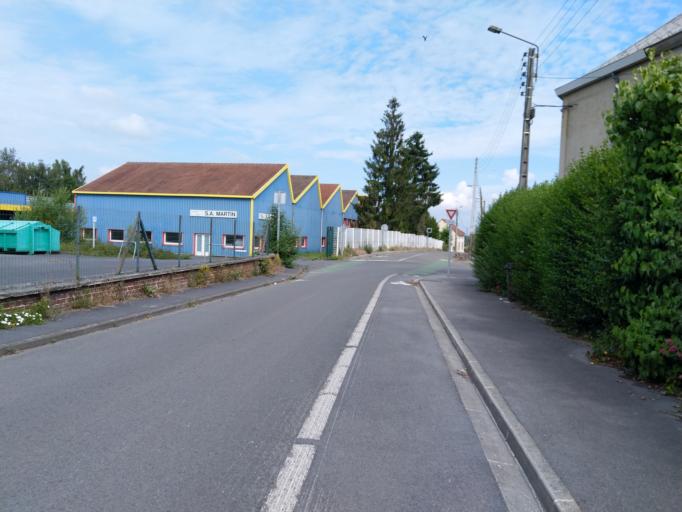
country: FR
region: Nord-Pas-de-Calais
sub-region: Departement du Nord
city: Maubeuge
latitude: 50.2675
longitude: 3.9759
